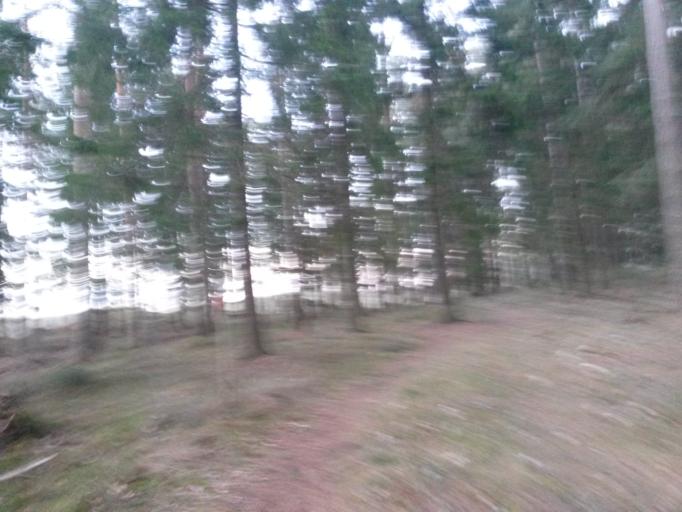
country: SE
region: Vaestra Goetaland
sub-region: Vargarda Kommun
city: Vargarda
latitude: 58.0419
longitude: 12.8186
